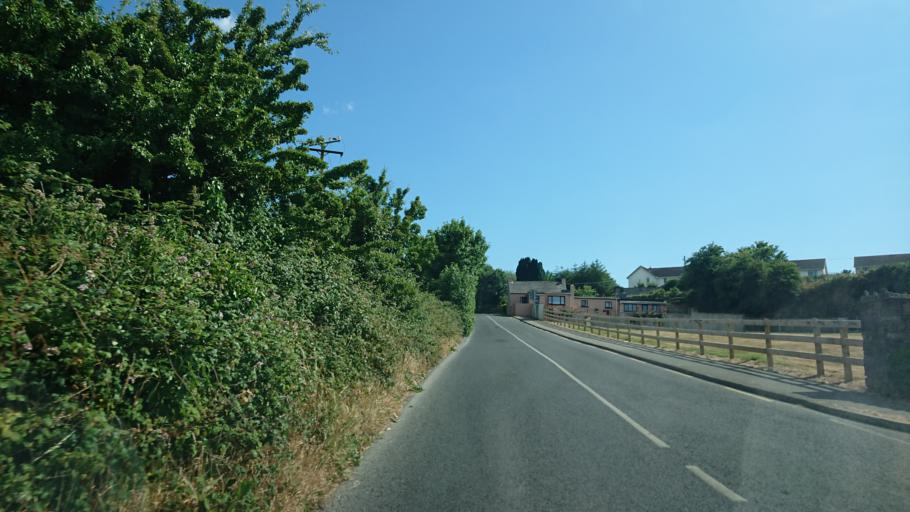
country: IE
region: Munster
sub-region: Waterford
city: Waterford
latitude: 52.2664
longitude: -7.1366
